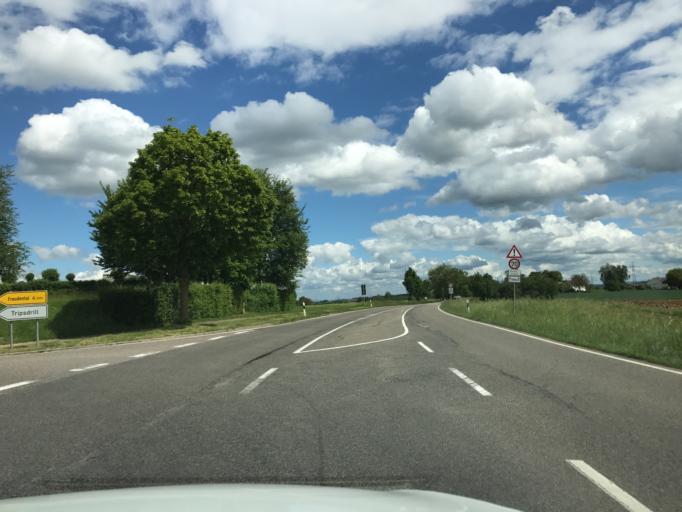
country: DE
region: Baden-Wuerttemberg
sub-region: Regierungsbezirk Stuttgart
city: Lochgau
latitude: 48.9856
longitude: 9.1006
